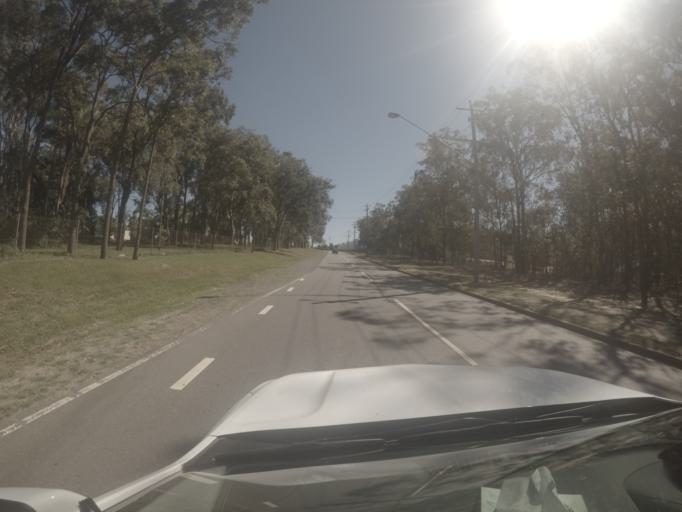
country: AU
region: Queensland
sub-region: Brisbane
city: Inala
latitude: -27.5735
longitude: 152.9683
